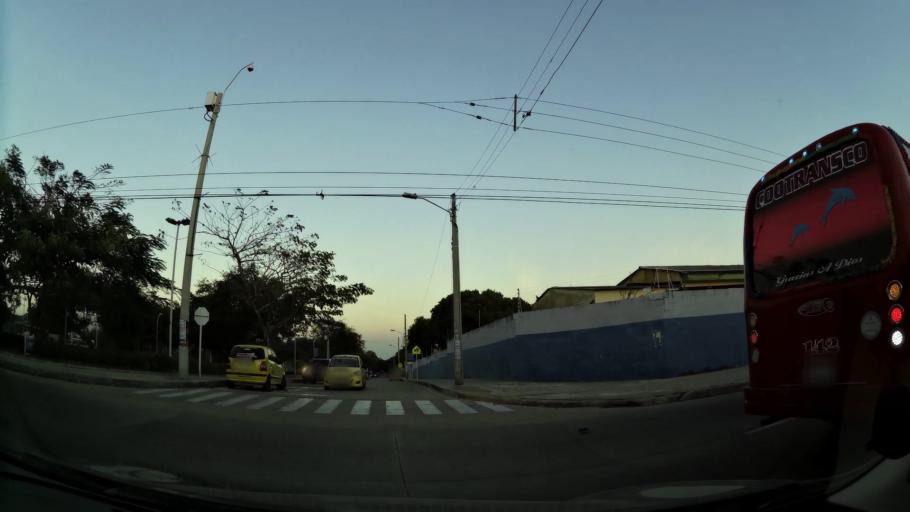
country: CO
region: Atlantico
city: Barranquilla
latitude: 10.9796
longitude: -74.8105
